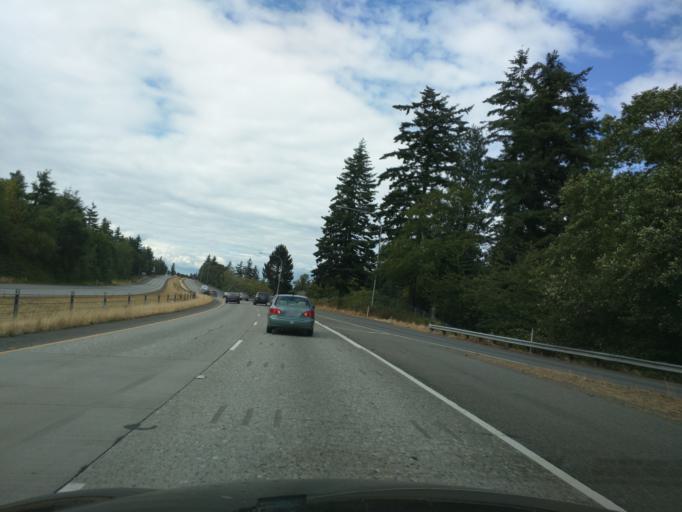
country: US
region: Washington
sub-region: Whatcom County
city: Bellingham
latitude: 48.7342
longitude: -122.4674
